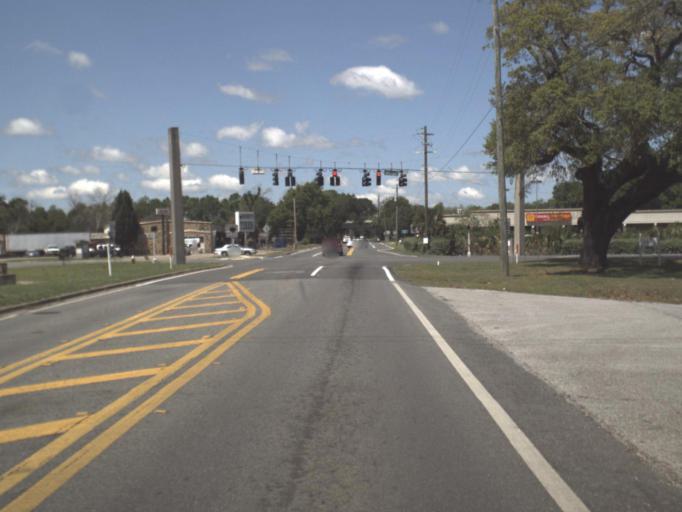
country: US
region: Florida
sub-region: Escambia County
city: West Pensacola
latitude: 30.4263
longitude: -87.2705
